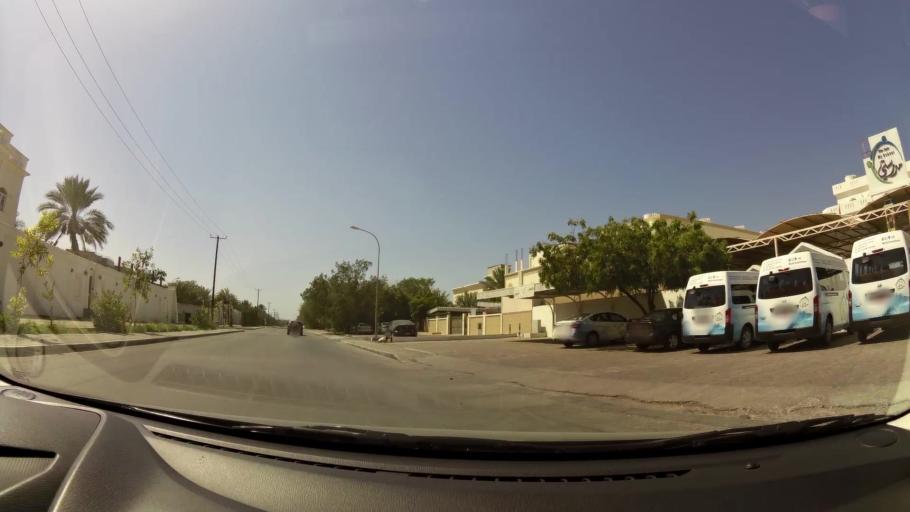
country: OM
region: Muhafazat Masqat
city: As Sib al Jadidah
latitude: 23.6301
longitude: 58.2226
